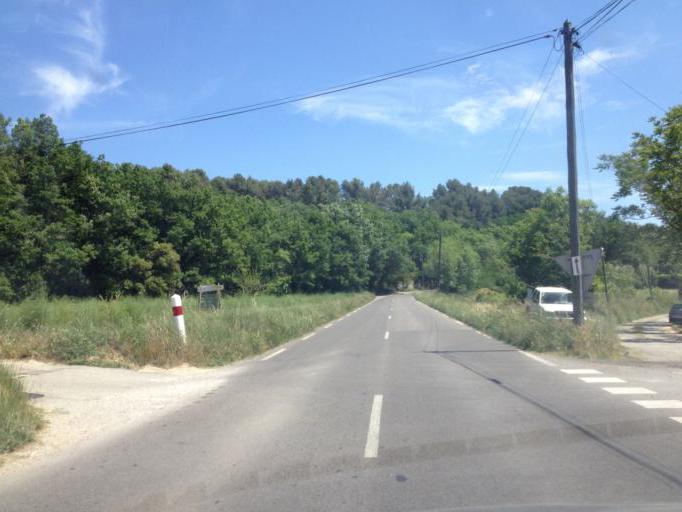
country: FR
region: Provence-Alpes-Cote d'Azur
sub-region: Departement du Vaucluse
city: Cadenet
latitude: 43.7405
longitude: 5.3479
